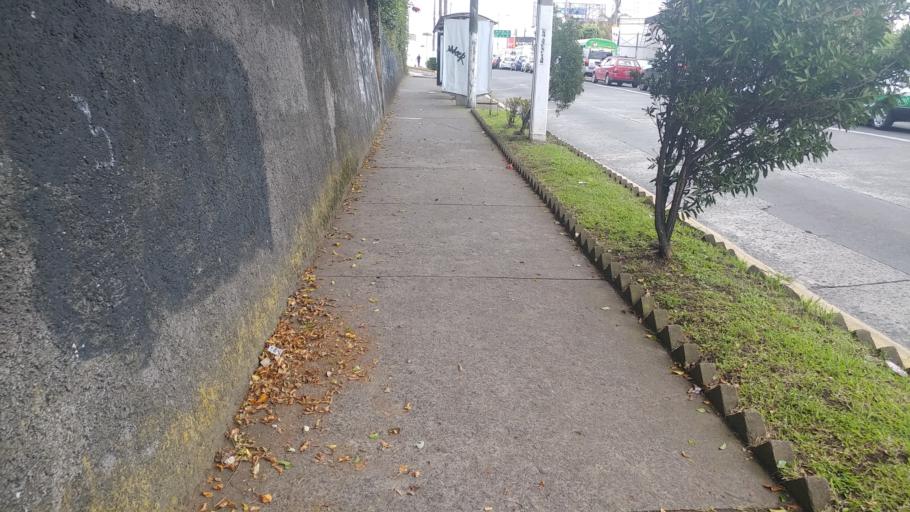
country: MX
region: Veracruz
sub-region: Xalapa
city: Xalapa de Enriquez
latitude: 19.5258
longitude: -96.9077
